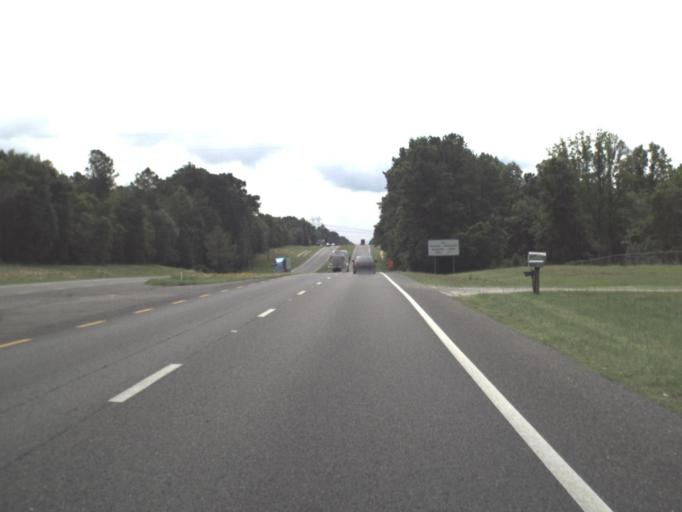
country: US
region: Florida
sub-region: Nassau County
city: Hilliard
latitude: 30.7555
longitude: -81.9629
